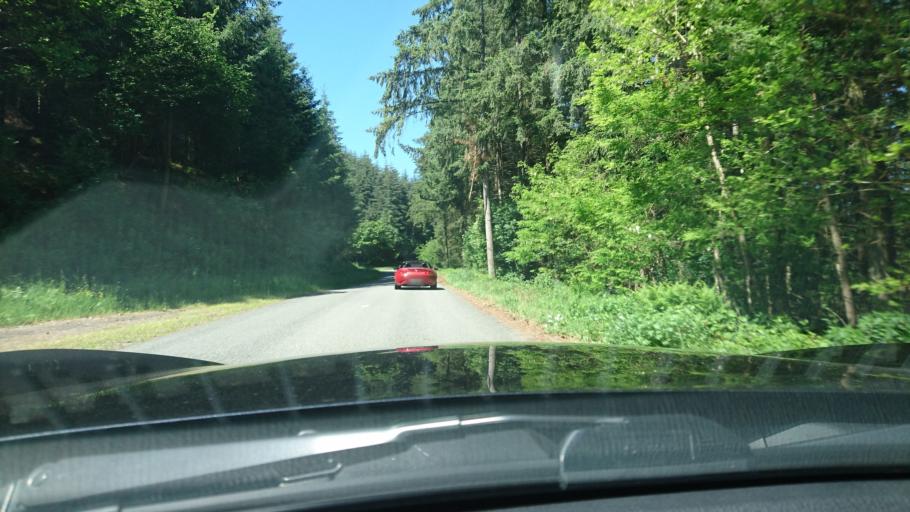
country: FR
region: Rhone-Alpes
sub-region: Departement de la Loire
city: Bussieres
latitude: 45.8619
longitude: 4.2498
